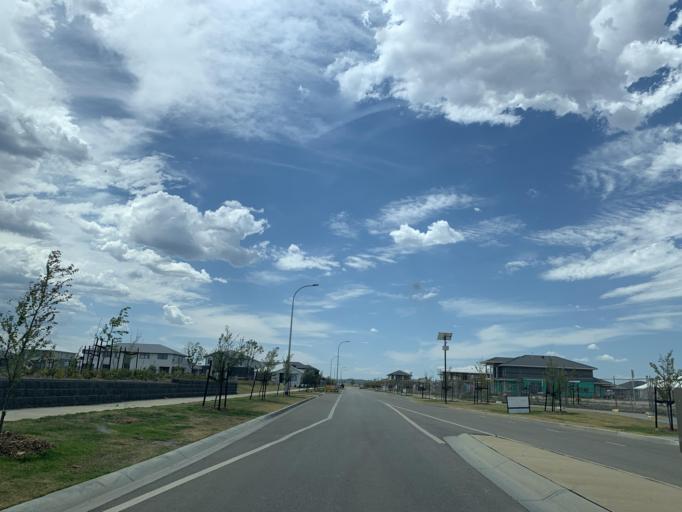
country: AU
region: Victoria
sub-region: Cardinia
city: Officer South
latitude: -38.1237
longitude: 145.3705
